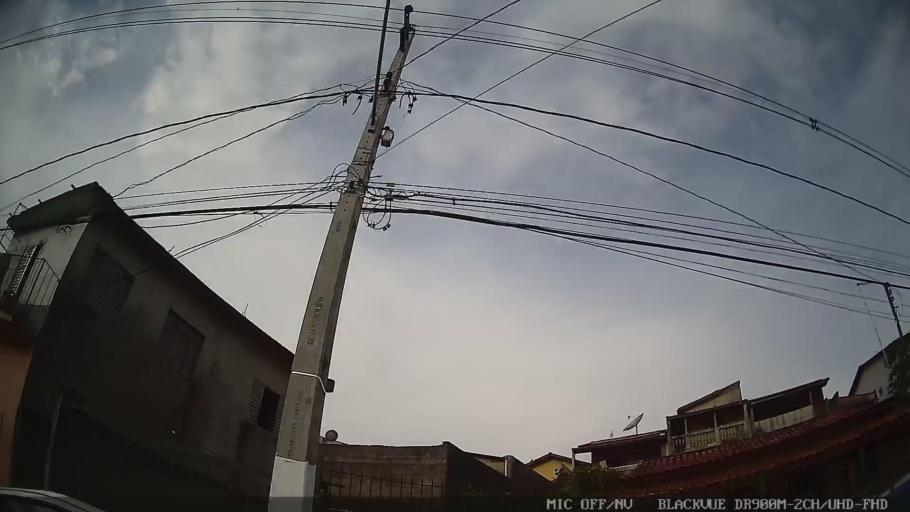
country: BR
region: Sao Paulo
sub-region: Braganca Paulista
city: Braganca Paulista
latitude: -22.9398
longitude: -46.5550
